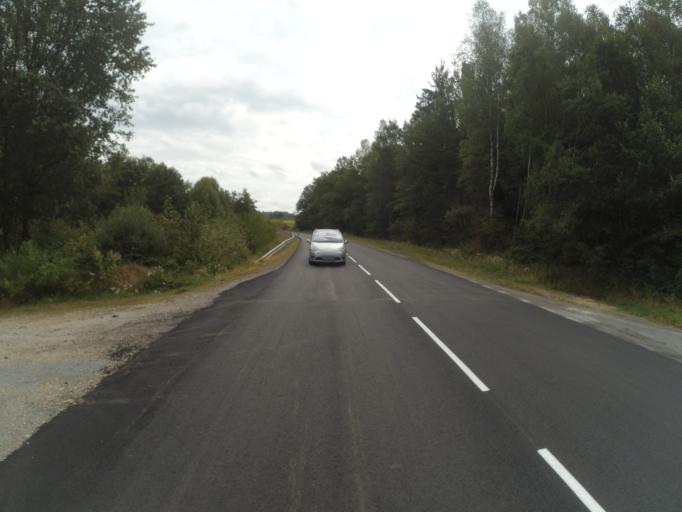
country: FR
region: Limousin
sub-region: Departement de la Creuse
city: La Courtine
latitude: 45.6526
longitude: 2.2417
